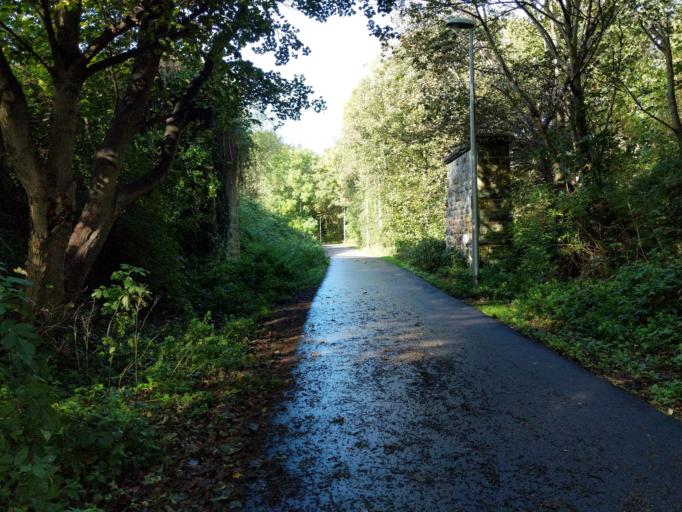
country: GB
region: Scotland
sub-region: Edinburgh
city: Edinburgh
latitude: 55.9714
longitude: -3.1943
